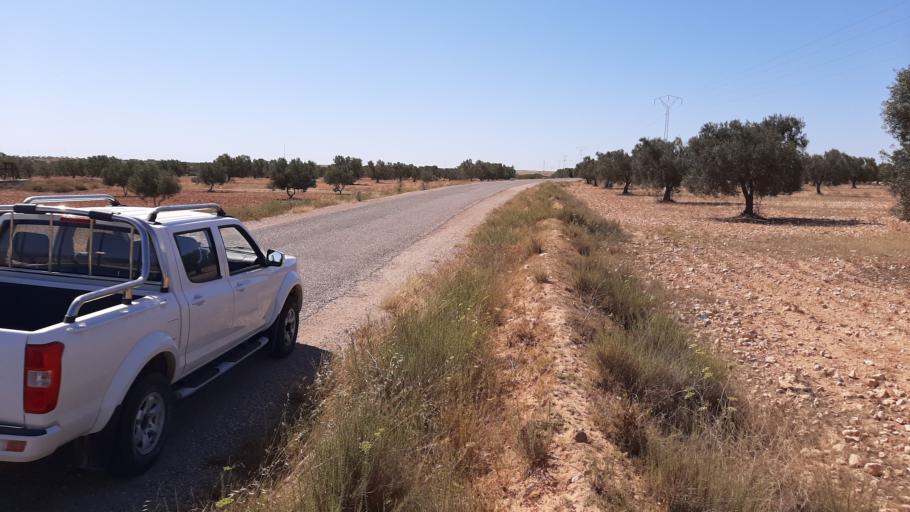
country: TN
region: Safaqis
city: Jabinyanah
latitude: 34.9785
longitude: 10.6892
